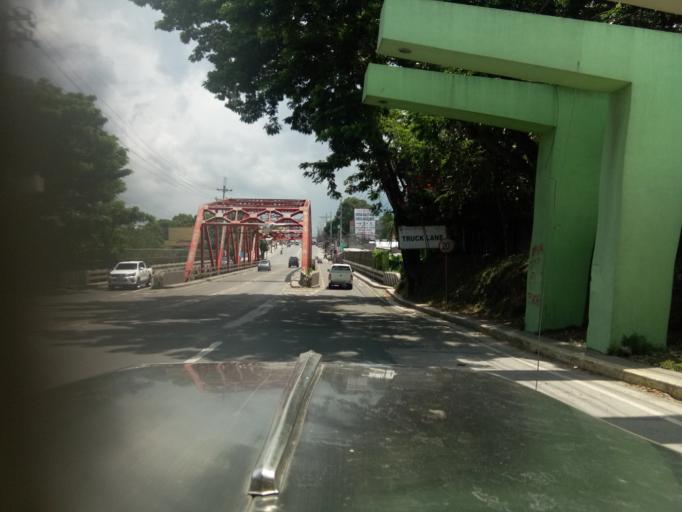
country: PH
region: Calabarzon
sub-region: Province of Cavite
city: Bulihan
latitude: 14.2857
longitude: 120.9928
